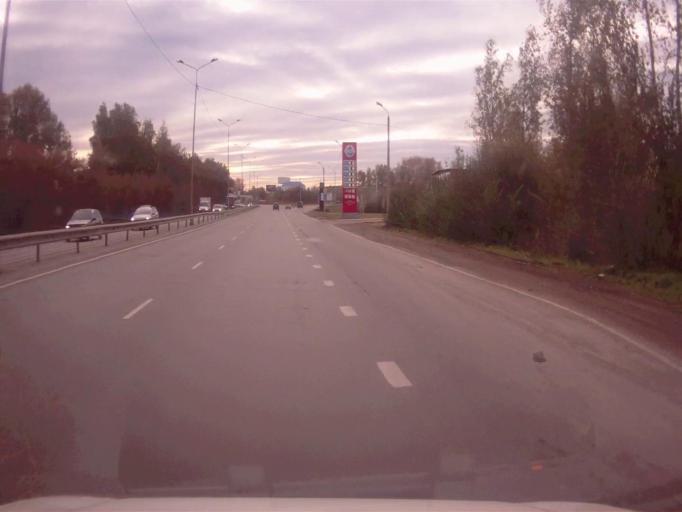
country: RU
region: Chelyabinsk
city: Novosineglazovskiy
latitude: 55.0836
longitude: 61.3944
